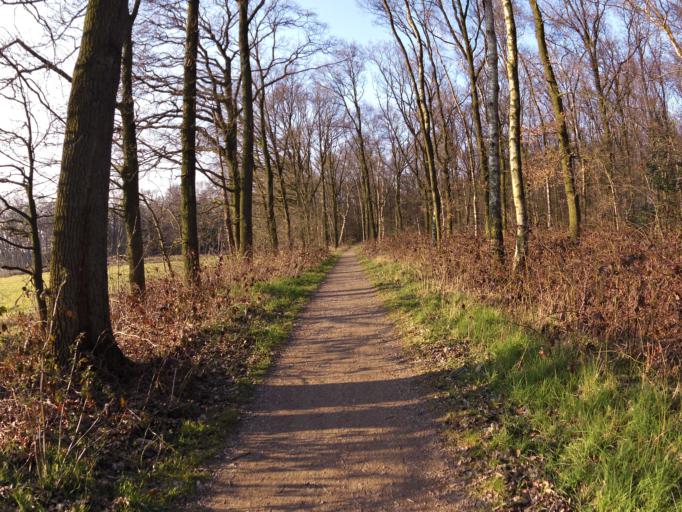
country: NL
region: North Brabant
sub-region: Gemeente Maasdonk
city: Geffen
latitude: 51.7043
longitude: 5.4023
